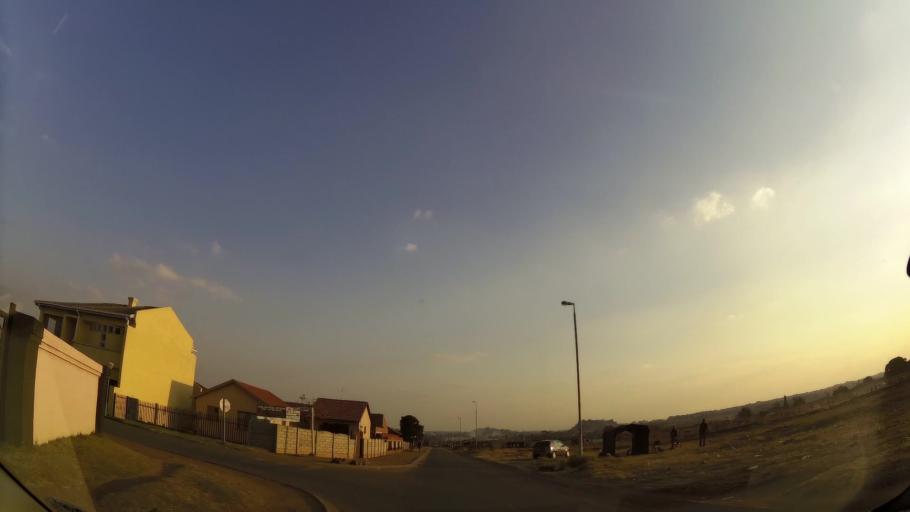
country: ZA
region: Gauteng
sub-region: Ekurhuleni Metropolitan Municipality
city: Benoni
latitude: -26.1597
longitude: 28.3766
